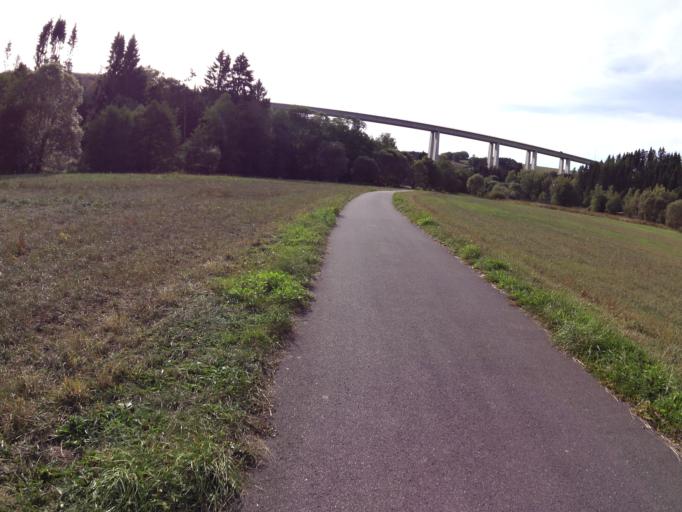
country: DE
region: Rheinland-Pfalz
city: Winterspelt
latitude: 50.2374
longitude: 6.1897
